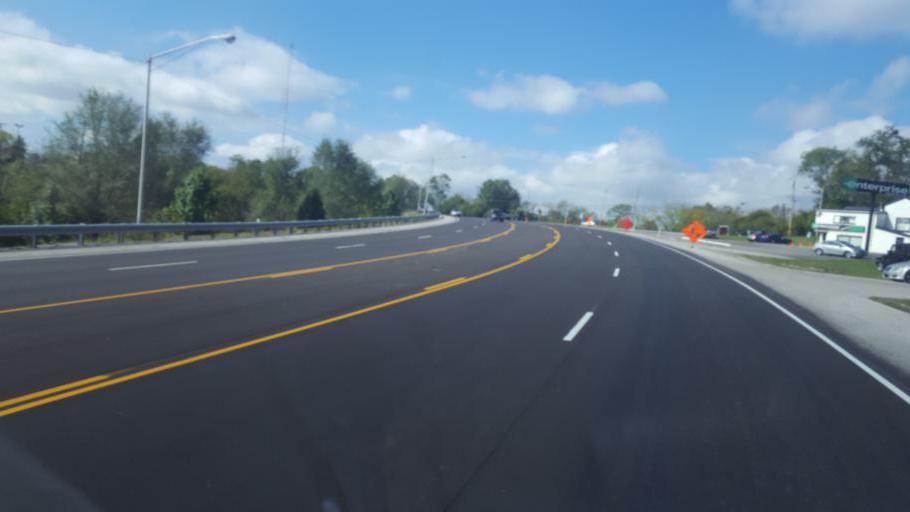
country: US
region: Ohio
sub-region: Brown County
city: Aberdeen
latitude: 38.6443
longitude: -83.7768
